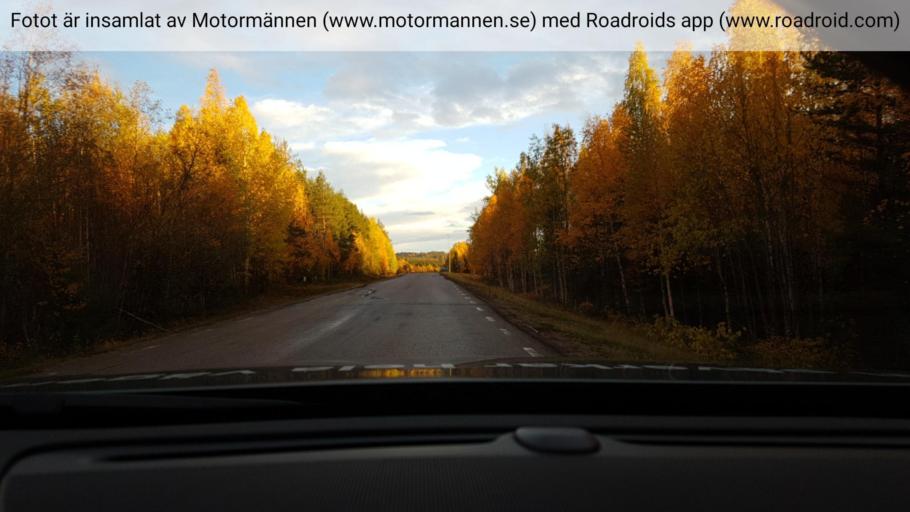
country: SE
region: Norrbotten
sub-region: Overkalix Kommun
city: OEverkalix
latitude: 66.6137
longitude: 22.7545
